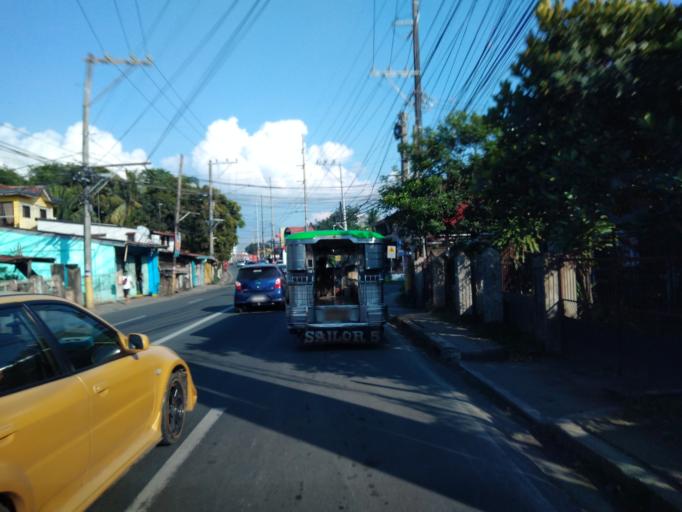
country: PH
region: Calabarzon
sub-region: Province of Laguna
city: Los Banos
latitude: 14.1792
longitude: 121.2374
